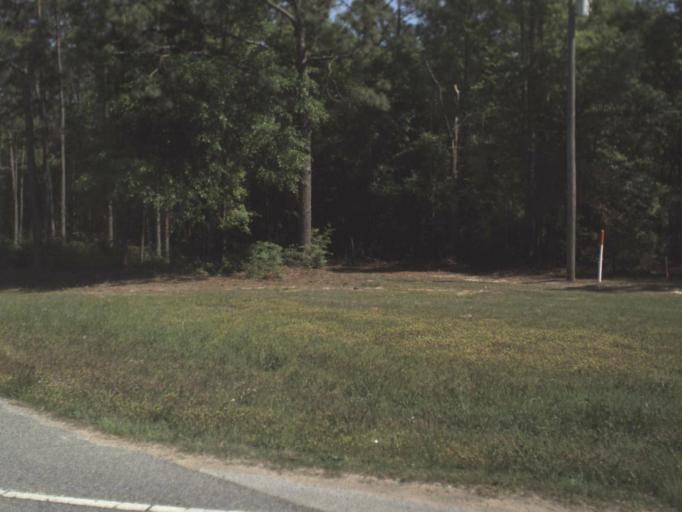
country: US
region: Florida
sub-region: Okaloosa County
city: Crestview
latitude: 30.7244
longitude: -86.6978
